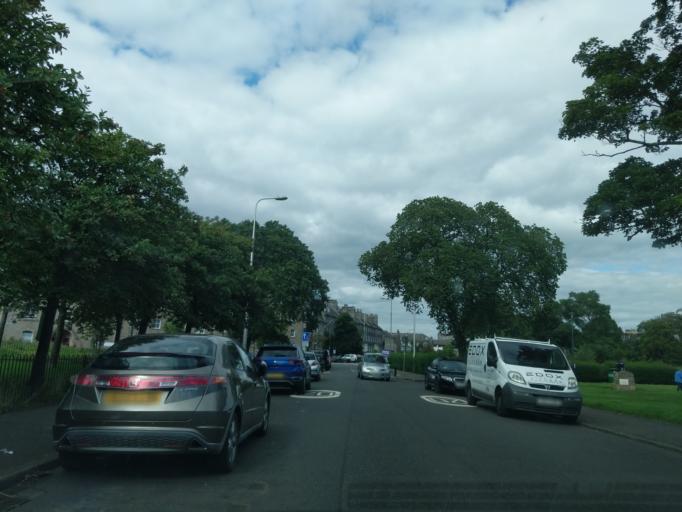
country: GB
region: Scotland
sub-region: West Lothian
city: Seafield
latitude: 55.9710
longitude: -3.1673
